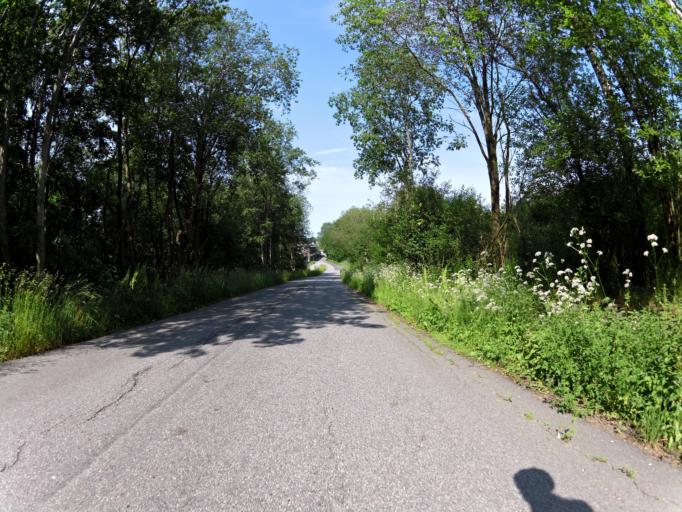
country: NO
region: Ostfold
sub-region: Sarpsborg
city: Sarpsborg
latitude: 59.2691
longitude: 11.1254
